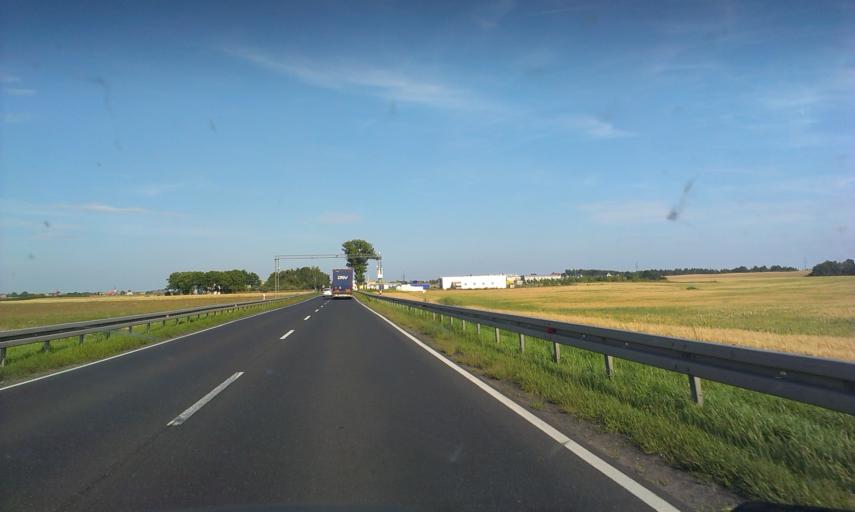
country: PL
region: Kujawsko-Pomorskie
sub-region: Powiat nakielski
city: Naklo nad Notecia
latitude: 53.1450
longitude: 17.5498
